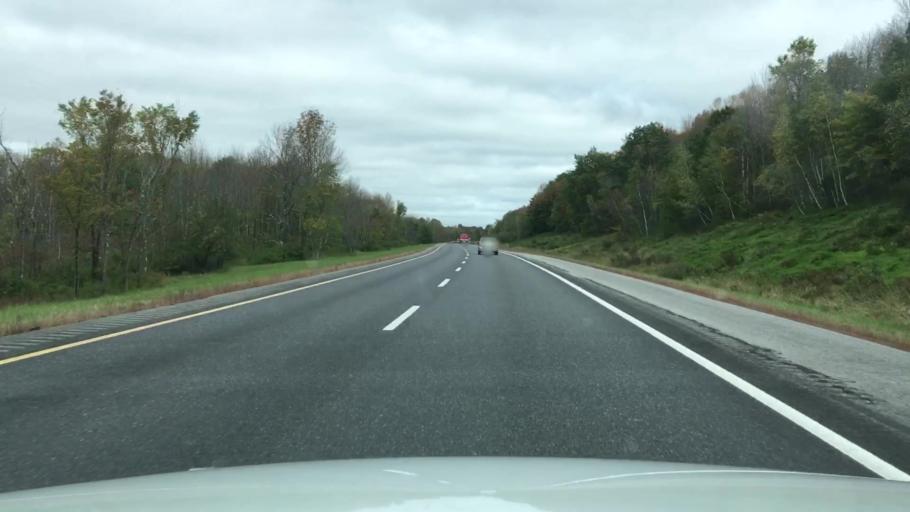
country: US
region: Maine
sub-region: Sagadahoc County
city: Richmond
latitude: 44.0693
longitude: -69.8789
